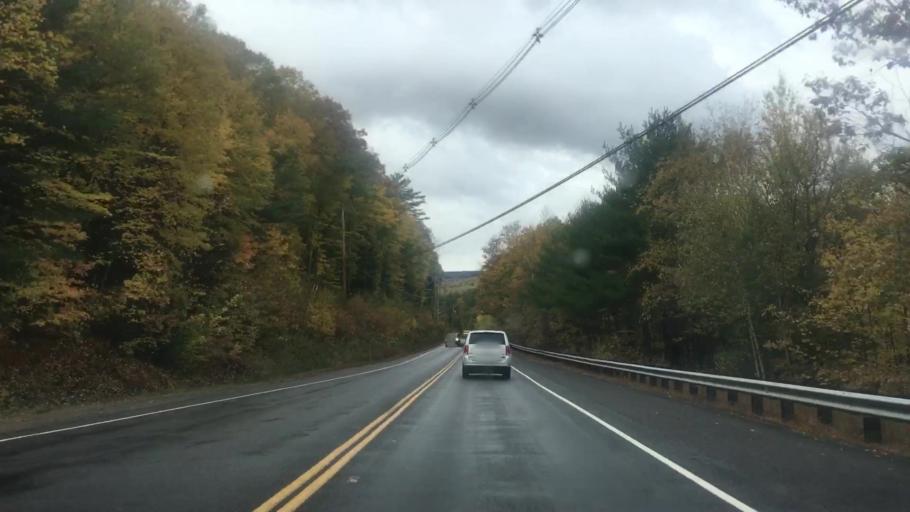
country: US
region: New Hampshire
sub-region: Carroll County
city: Wolfeboro
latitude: 43.5382
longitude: -71.2871
